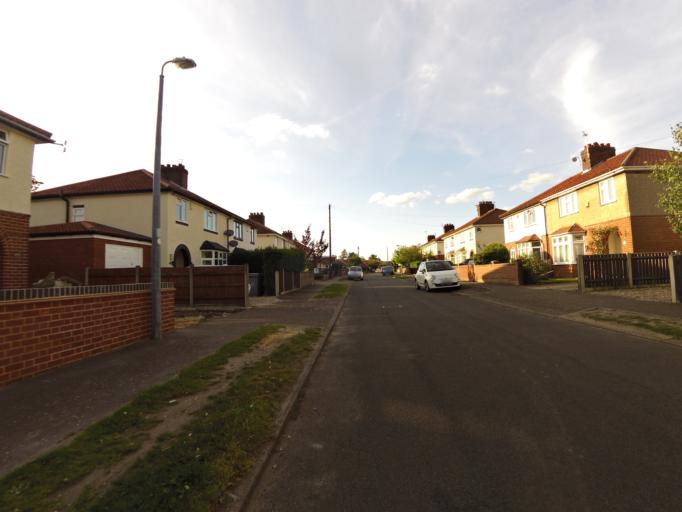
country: GB
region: England
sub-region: Norfolk
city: Norwich
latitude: 52.6571
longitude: 1.2723
